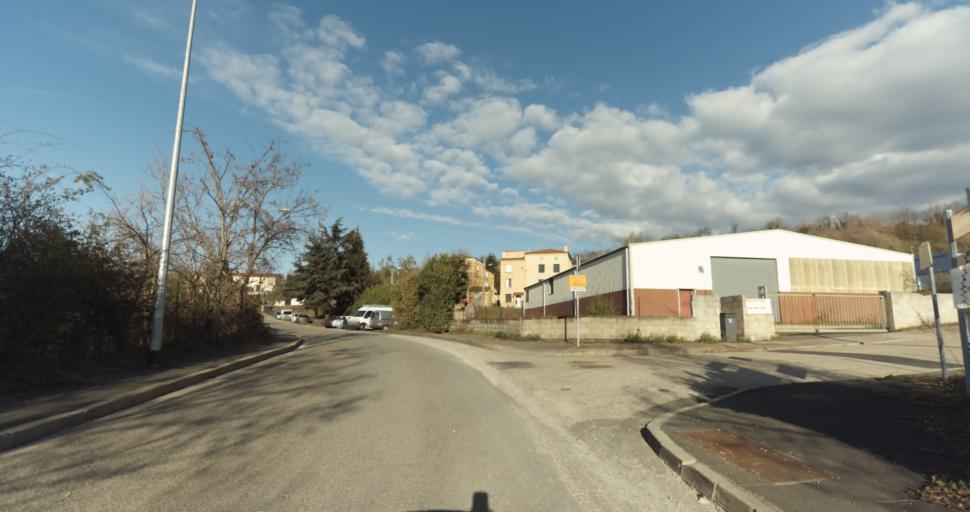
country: FR
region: Rhone-Alpes
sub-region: Departement de la Loire
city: La Talaudiere
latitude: 45.4557
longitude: 4.4236
